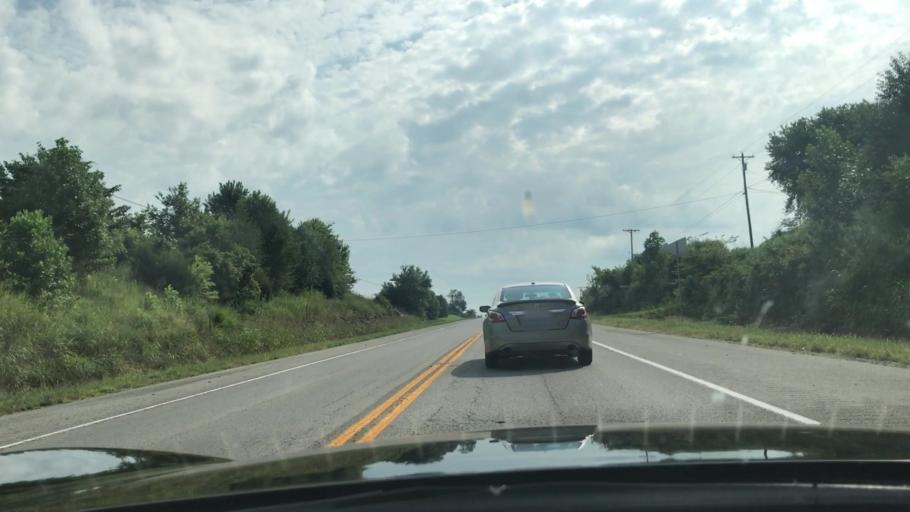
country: US
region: Kentucky
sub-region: Green County
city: Greensburg
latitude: 37.2954
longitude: -85.4636
